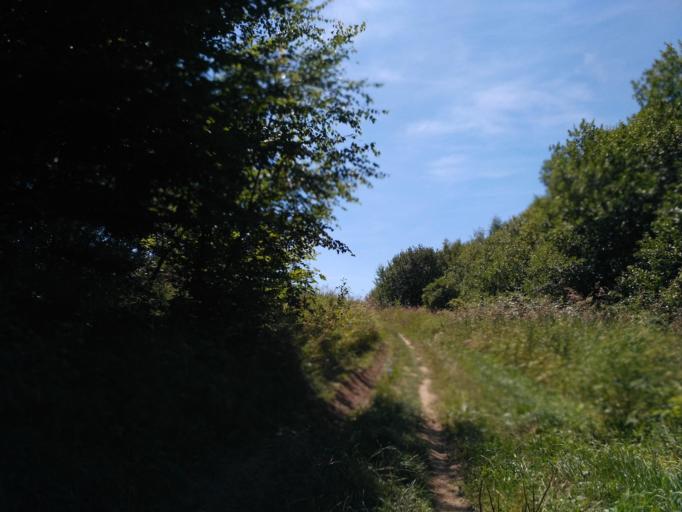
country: PL
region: Subcarpathian Voivodeship
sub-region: Powiat sanocki
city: Bukowsko
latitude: 49.5115
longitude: 22.0551
